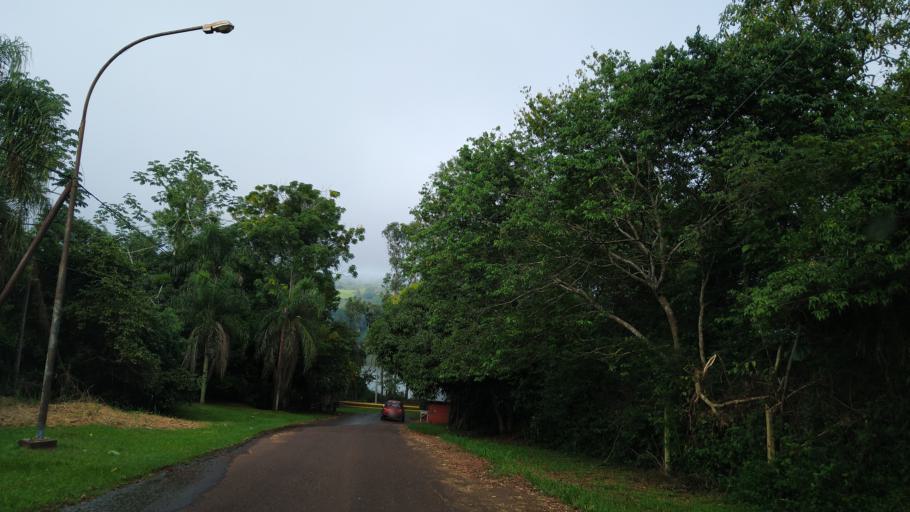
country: AR
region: Misiones
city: Caraguatay
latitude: -26.5686
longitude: -54.7981
